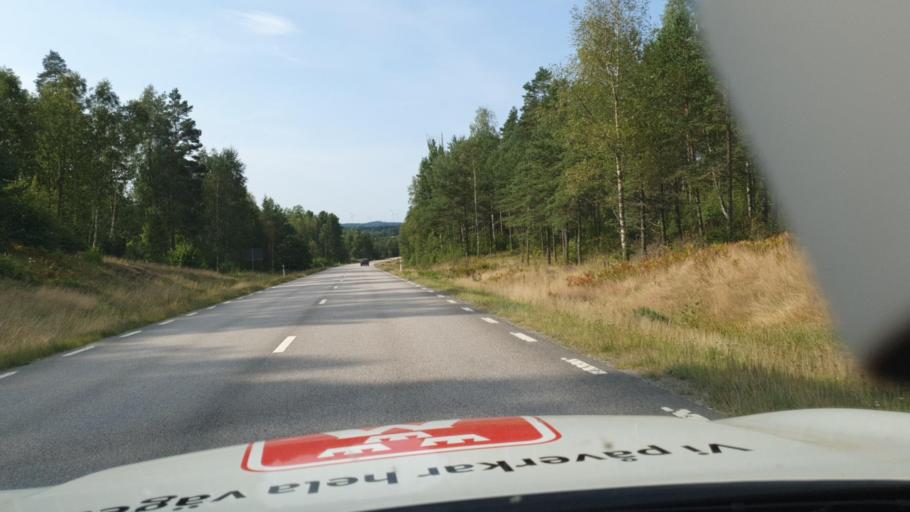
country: SE
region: Vaestra Goetaland
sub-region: Dals-Ed Kommun
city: Ed
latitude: 58.8969
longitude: 11.9322
